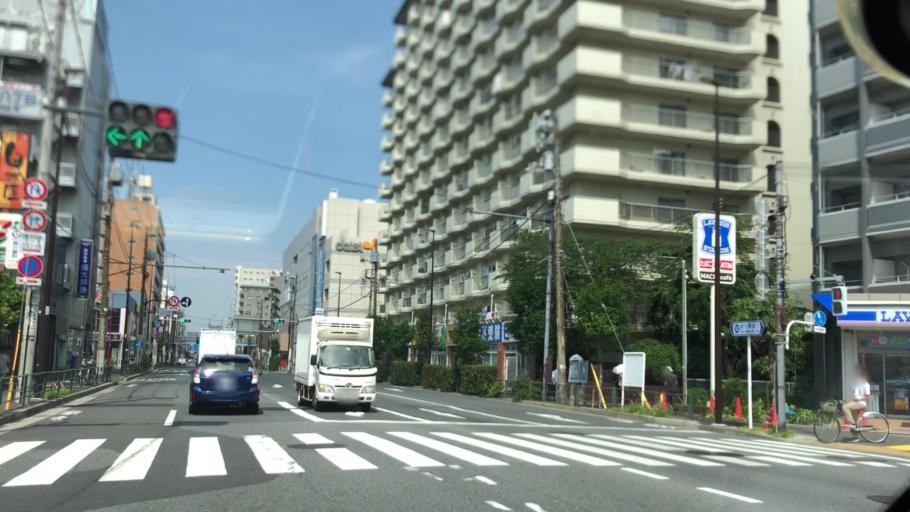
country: JP
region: Tokyo
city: Urayasu
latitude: 35.6906
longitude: 139.8443
